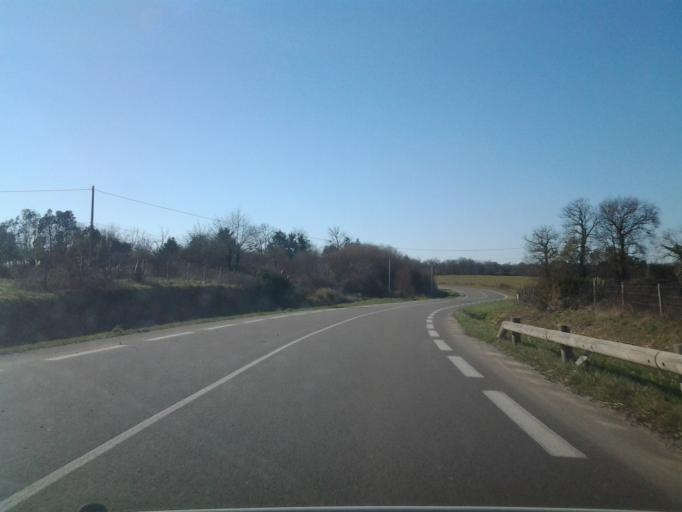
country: FR
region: Pays de la Loire
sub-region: Departement de la Vendee
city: Olonne-sur-Mer
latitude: 46.5387
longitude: -1.7452
